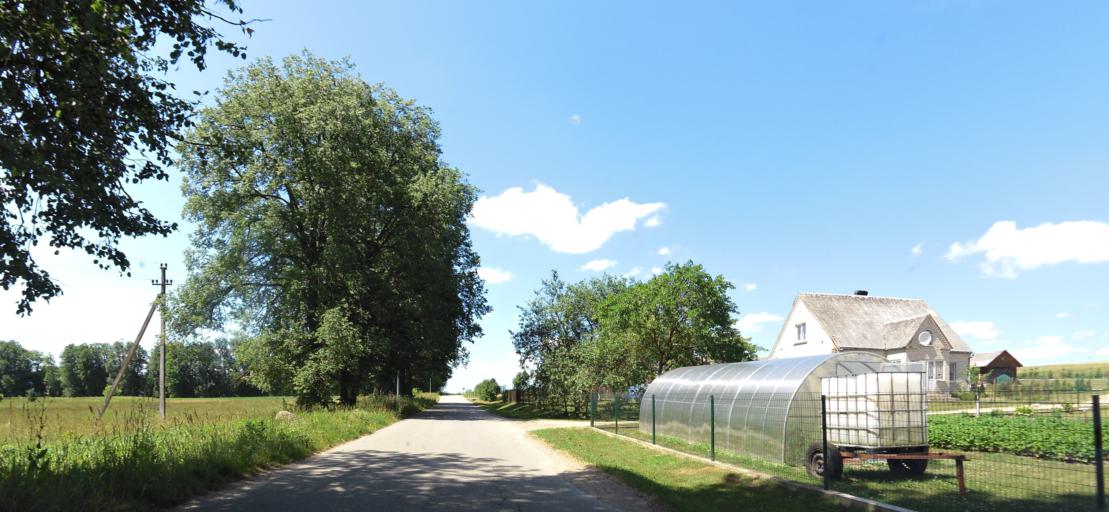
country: LT
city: Nemencine
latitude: 54.8755
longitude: 25.5416
